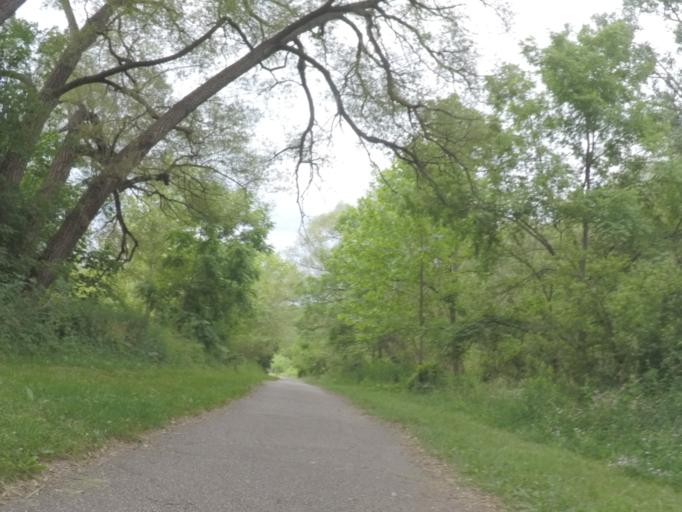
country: CA
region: Ontario
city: Etobicoke
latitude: 43.6589
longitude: -79.5575
